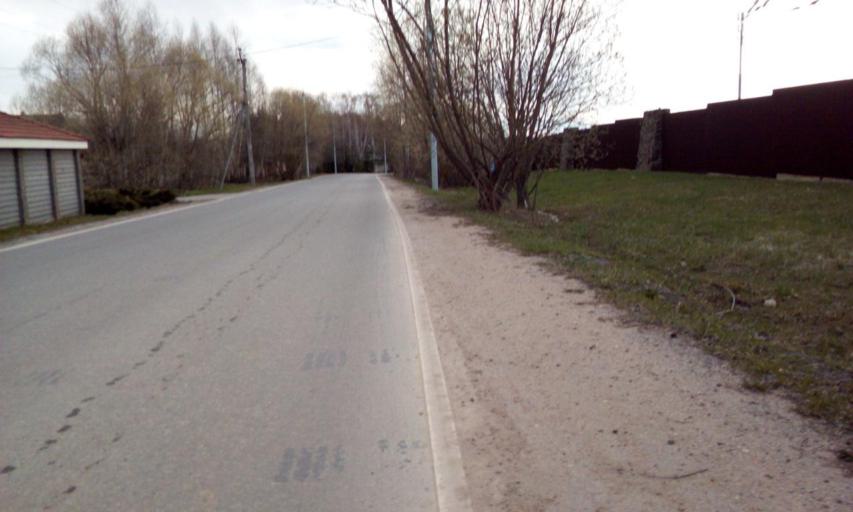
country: RU
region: Moskovskaya
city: Annino
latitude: 55.5239
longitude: 37.2576
